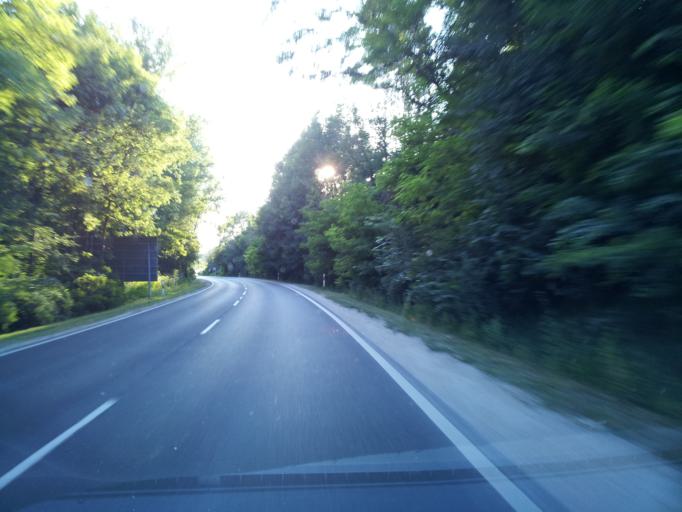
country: HU
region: Komarom-Esztergom
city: Tatabanya
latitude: 47.5714
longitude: 18.4332
